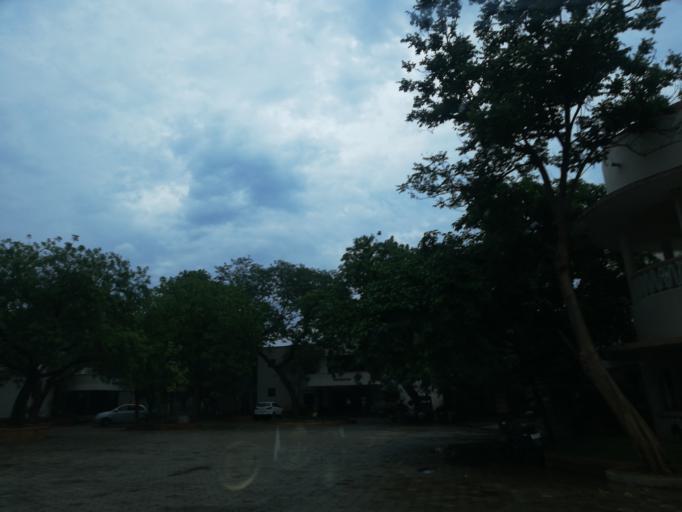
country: IN
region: Andhra Pradesh
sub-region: Guntur
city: Macherla
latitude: 16.6106
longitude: 79.2958
